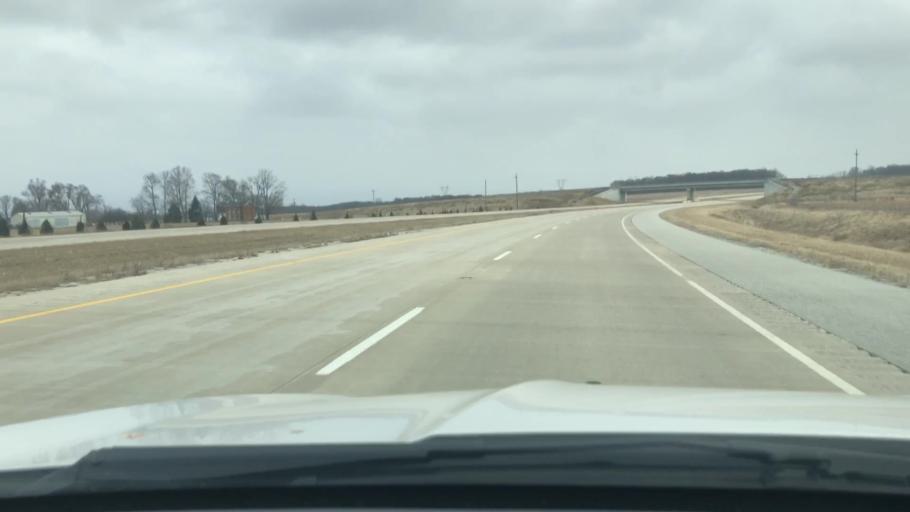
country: US
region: Indiana
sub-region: Carroll County
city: Delphi
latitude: 40.6215
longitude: -86.6245
